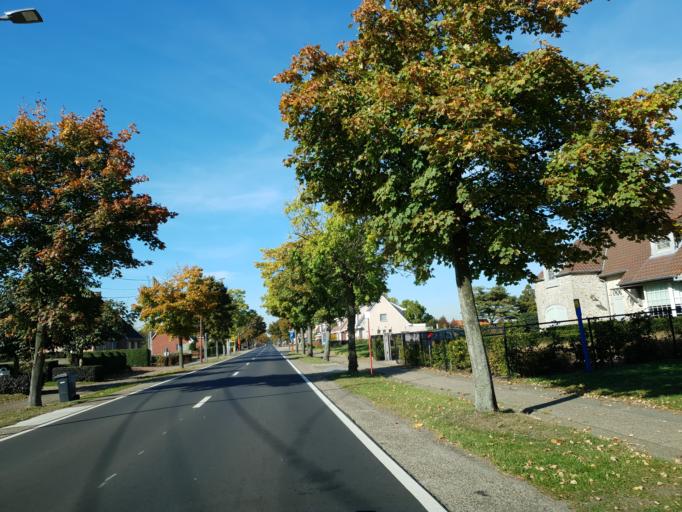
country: BE
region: Flanders
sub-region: Provincie Antwerpen
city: Stabroek
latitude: 51.3191
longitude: 4.3913
